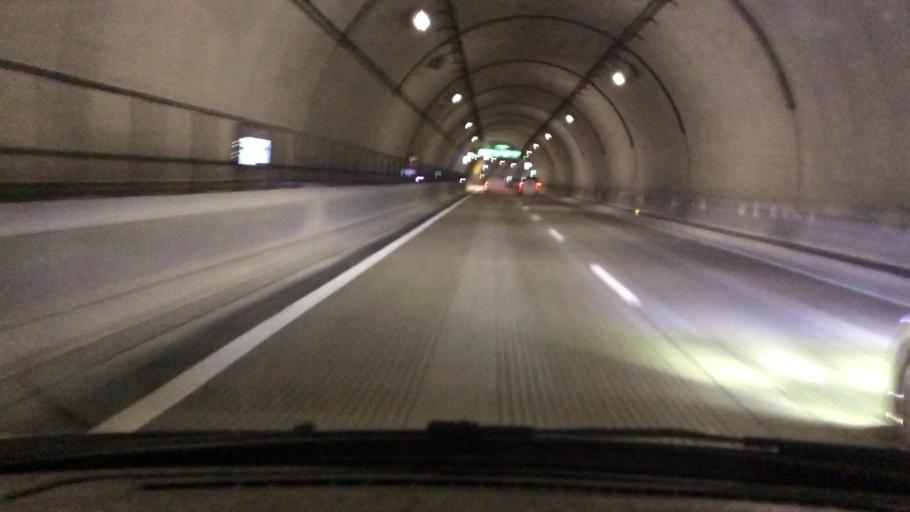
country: JP
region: Hyogo
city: Sandacho
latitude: 34.8266
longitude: 135.2585
